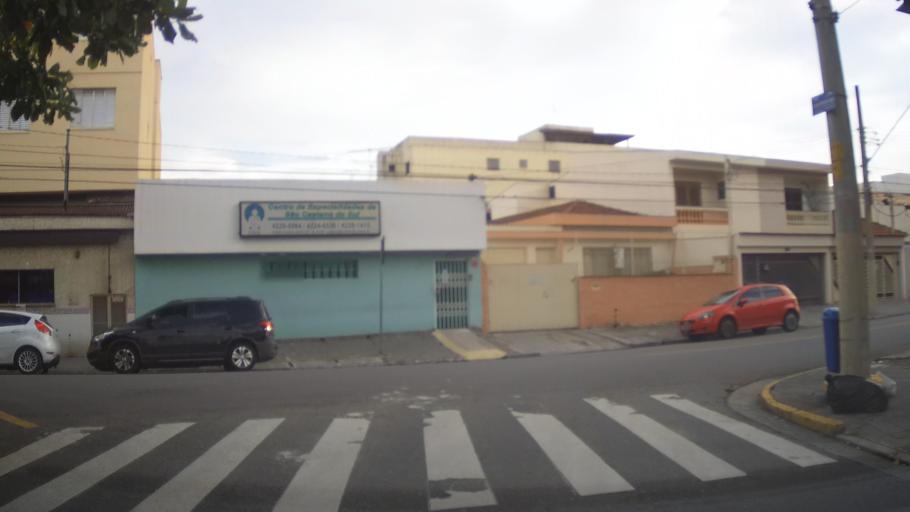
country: BR
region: Sao Paulo
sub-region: Sao Caetano Do Sul
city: Sao Caetano do Sul
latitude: -23.6243
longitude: -46.5578
